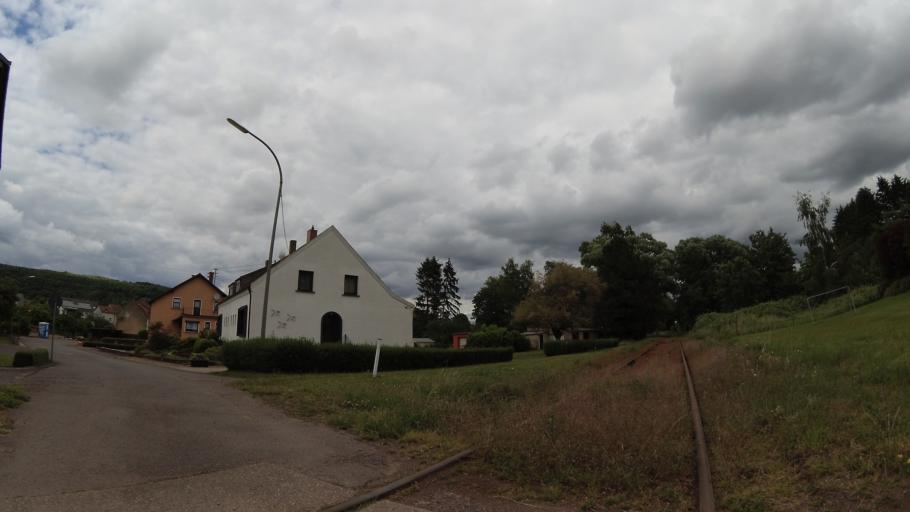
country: DE
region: Saarland
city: Saarwellingen
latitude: 49.3882
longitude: 6.8345
